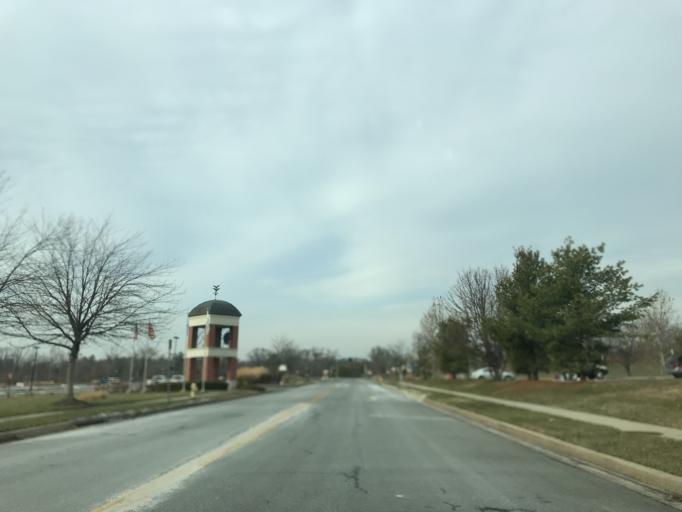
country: US
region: Maryland
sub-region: Harford County
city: Riverside
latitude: 39.4673
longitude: -76.2342
